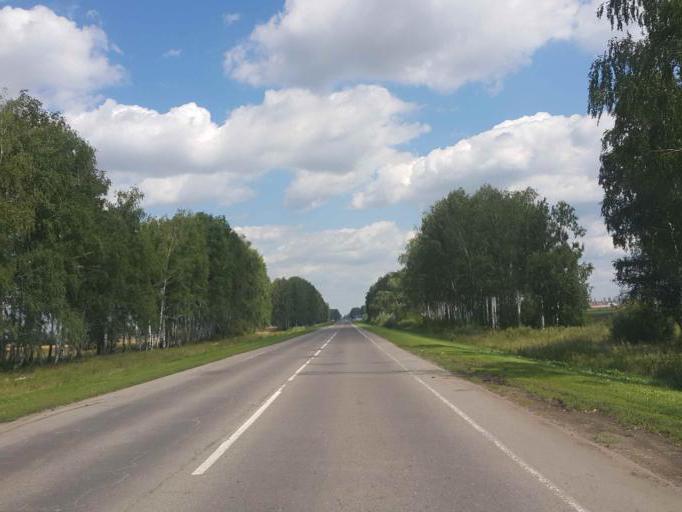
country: RU
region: Tambov
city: Goreloye
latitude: 53.0440
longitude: 41.4710
